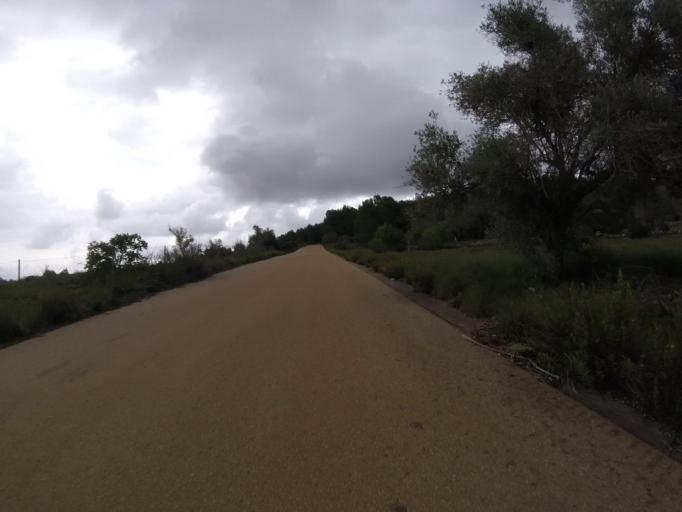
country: ES
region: Valencia
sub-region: Provincia de Castello
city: Benlloch
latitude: 40.2033
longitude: 0.0711
